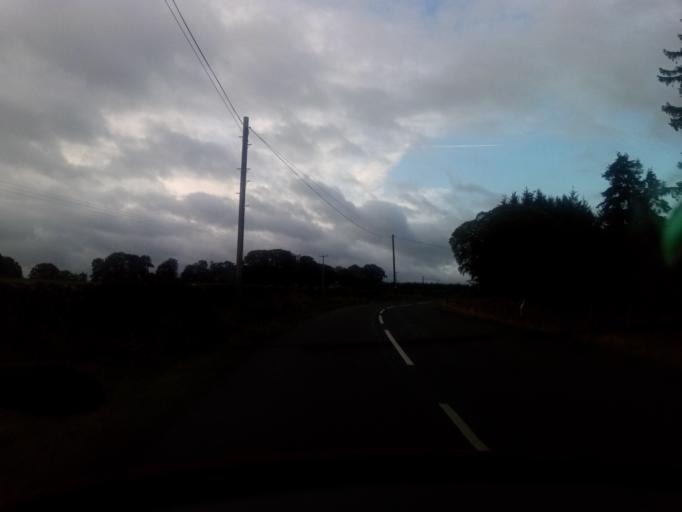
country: GB
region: Scotland
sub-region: The Scottish Borders
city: Jedburgh
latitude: 55.4182
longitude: -2.6316
